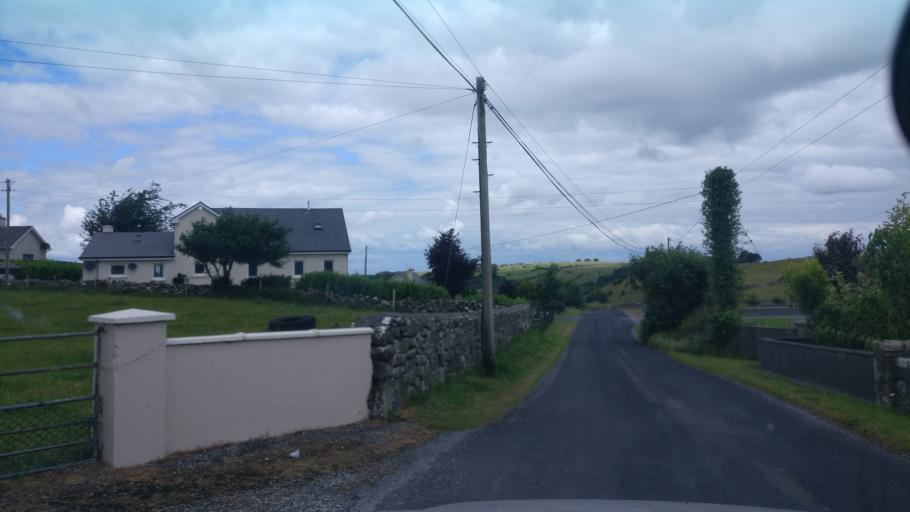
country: IE
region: Connaught
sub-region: County Galway
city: Loughrea
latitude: 53.1741
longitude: -8.5557
